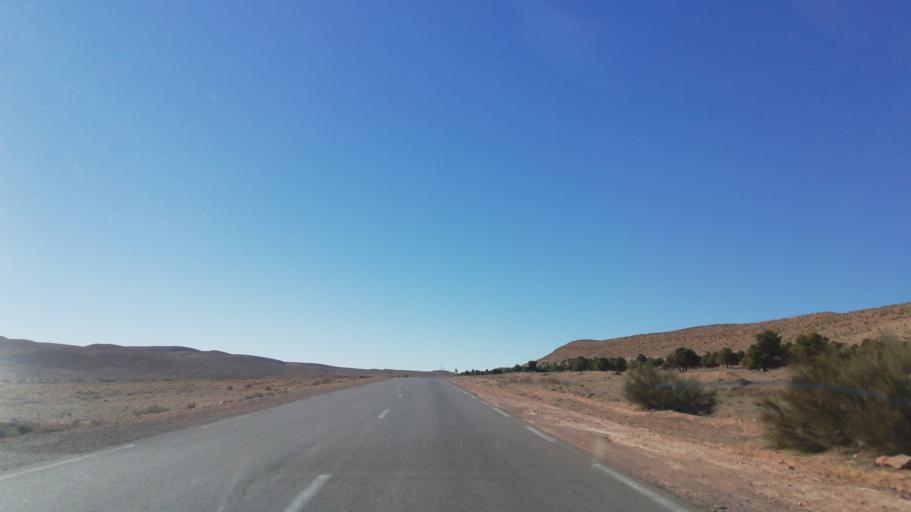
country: DZ
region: El Bayadh
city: El Bayadh
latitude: 33.6819
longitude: 1.4546
